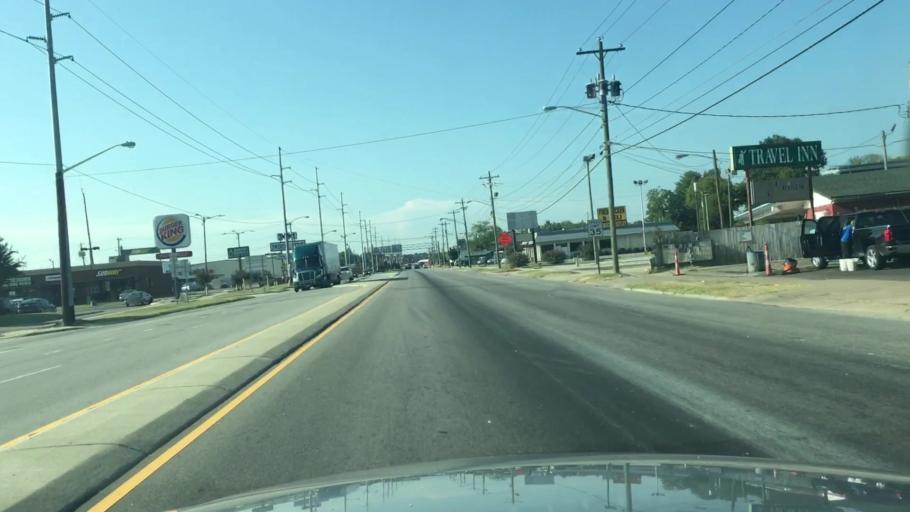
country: US
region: North Carolina
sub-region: Cumberland County
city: Fayetteville
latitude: 35.0519
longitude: -78.8645
